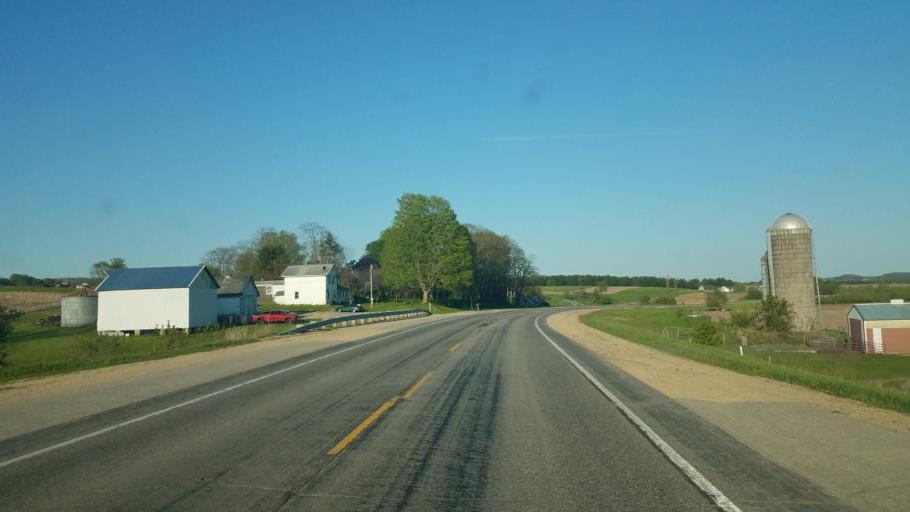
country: US
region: Wisconsin
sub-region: Vernon County
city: Hillsboro
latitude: 43.6601
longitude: -90.3793
